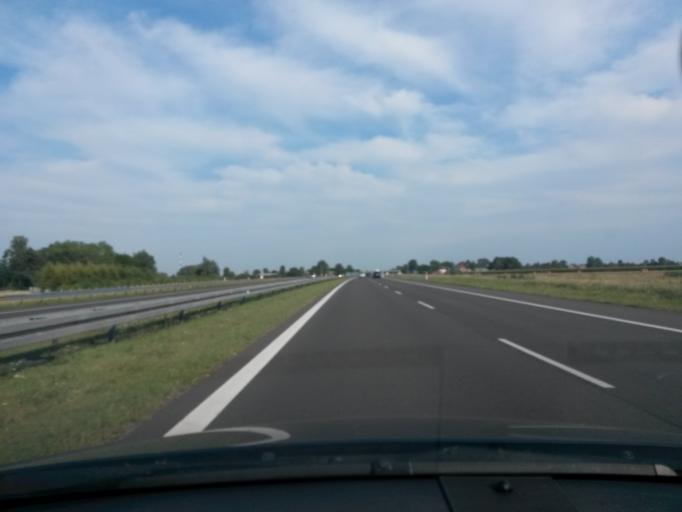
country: PL
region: Greater Poland Voivodeship
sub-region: Powiat slupecki
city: Slupca
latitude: 52.2404
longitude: 17.8788
